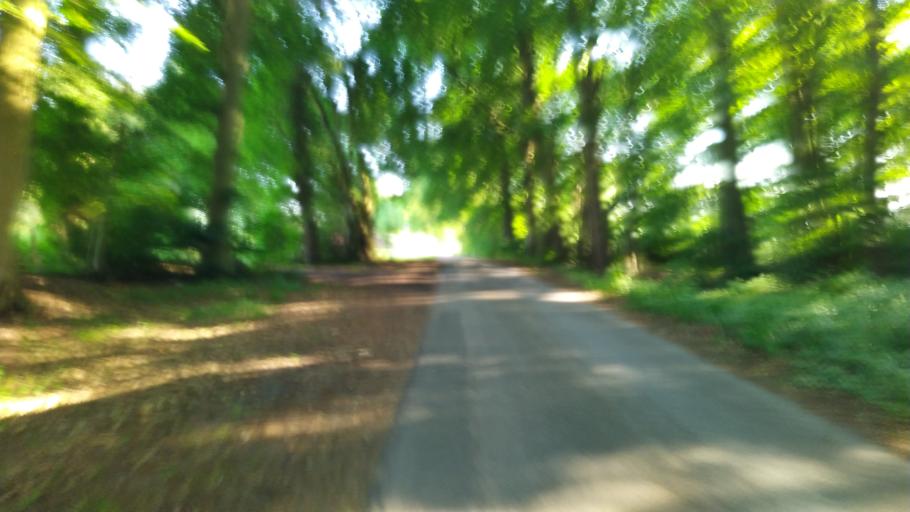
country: DE
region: Lower Saxony
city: Lintig
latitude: 53.5948
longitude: 8.9293
